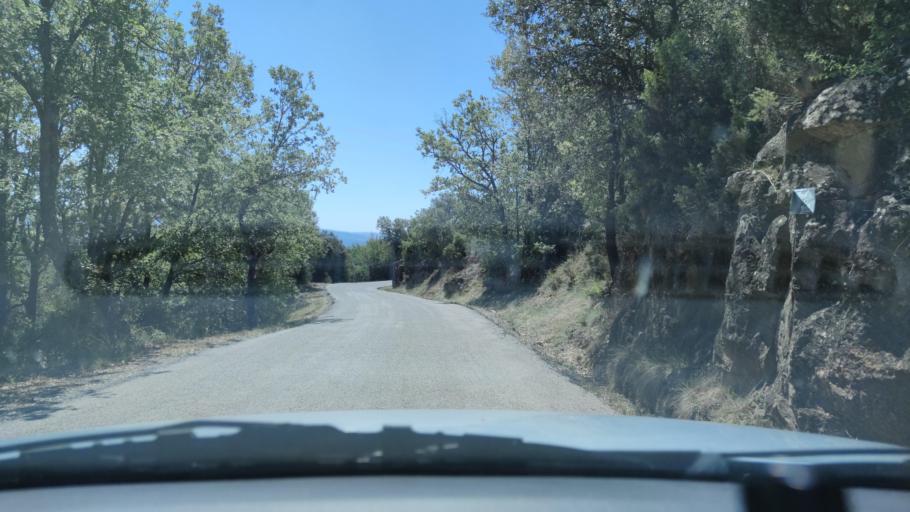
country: ES
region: Catalonia
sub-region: Provincia de Lleida
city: Tora de Riubregos
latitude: 41.8750
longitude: 1.4358
